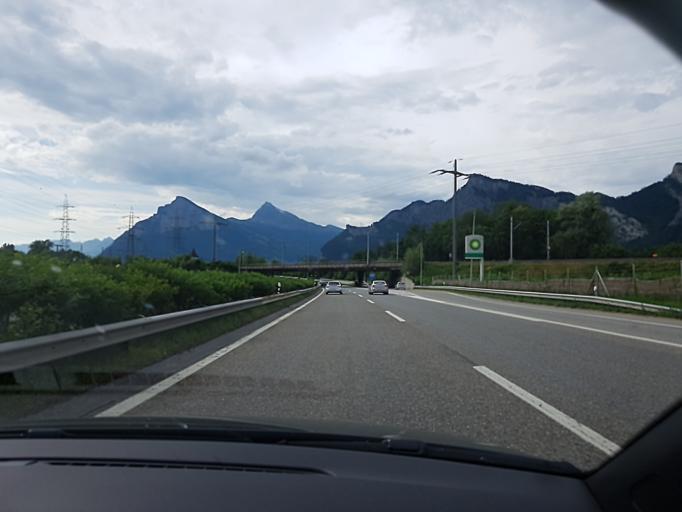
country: CH
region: Saint Gallen
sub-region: Wahlkreis Sarganserland
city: Bad Ragaz
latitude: 47.0088
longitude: 9.5159
